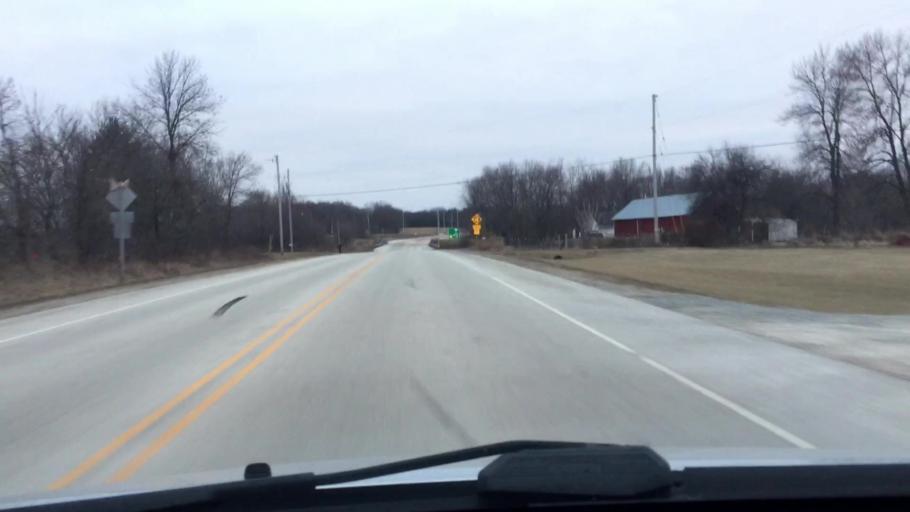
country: US
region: Wisconsin
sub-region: Jefferson County
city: Watertown
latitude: 43.1565
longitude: -88.7488
